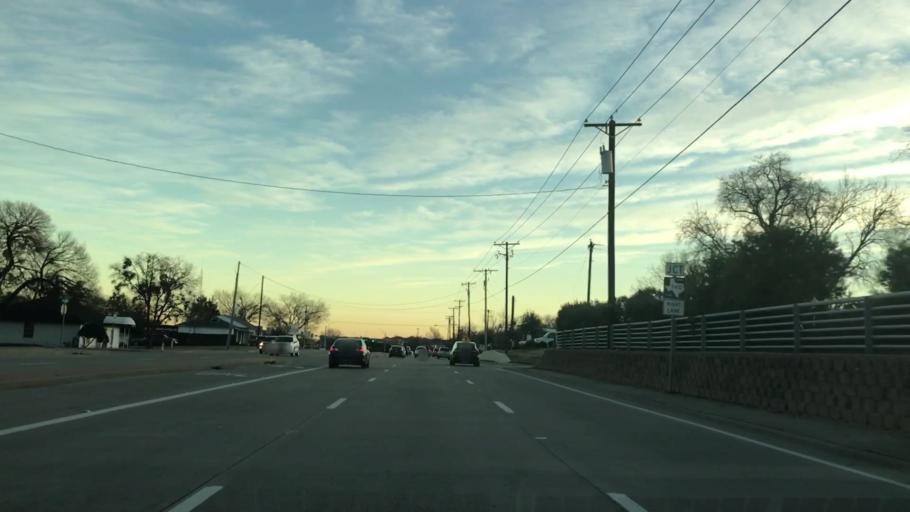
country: US
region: Texas
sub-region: Rockwall County
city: Rockwall
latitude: 32.9236
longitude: -96.4605
